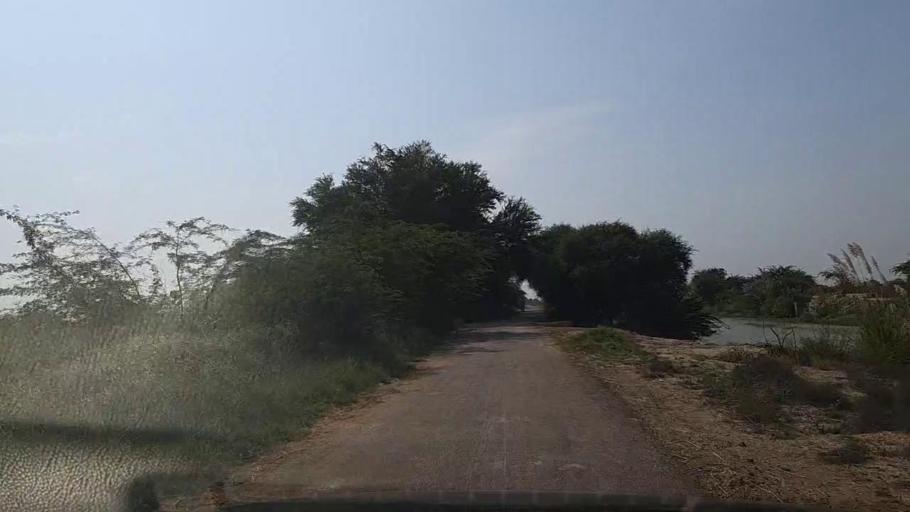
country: PK
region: Sindh
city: Thatta
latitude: 24.8018
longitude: 67.8398
